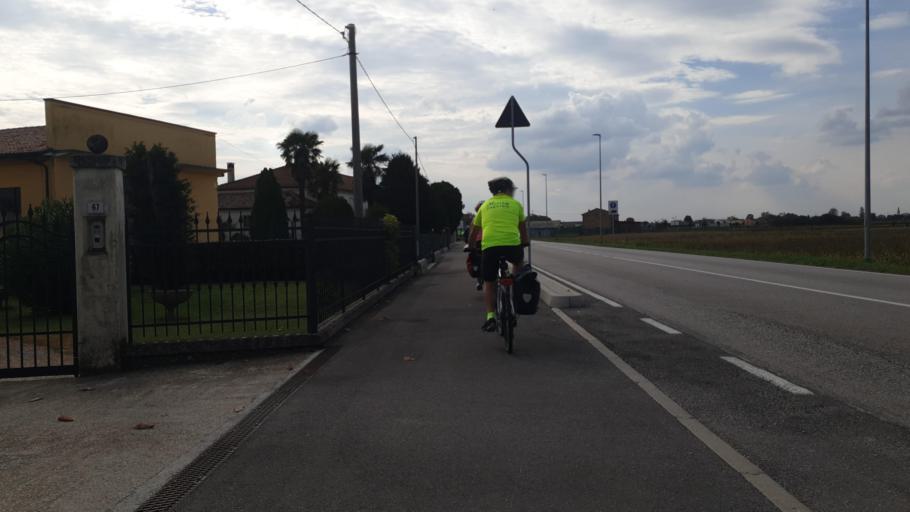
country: IT
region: Veneto
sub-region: Provincia di Vicenza
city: Noventa Vicentina
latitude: 45.2872
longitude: 11.5316
